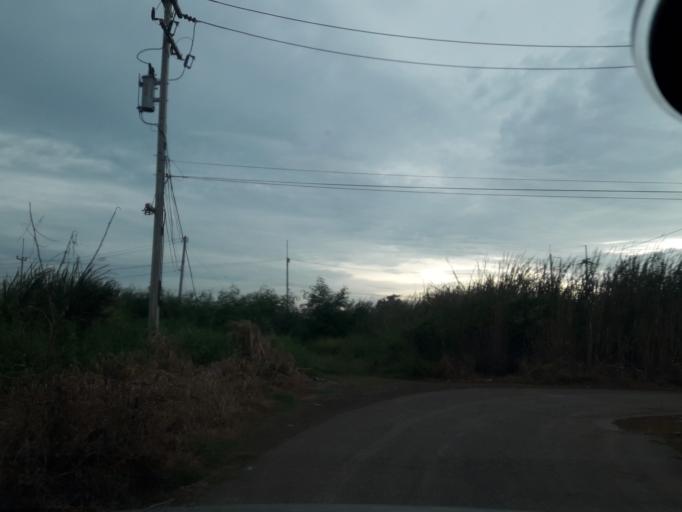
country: TH
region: Phra Nakhon Si Ayutthaya
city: Wang Noi
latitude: 14.2623
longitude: 100.7811
